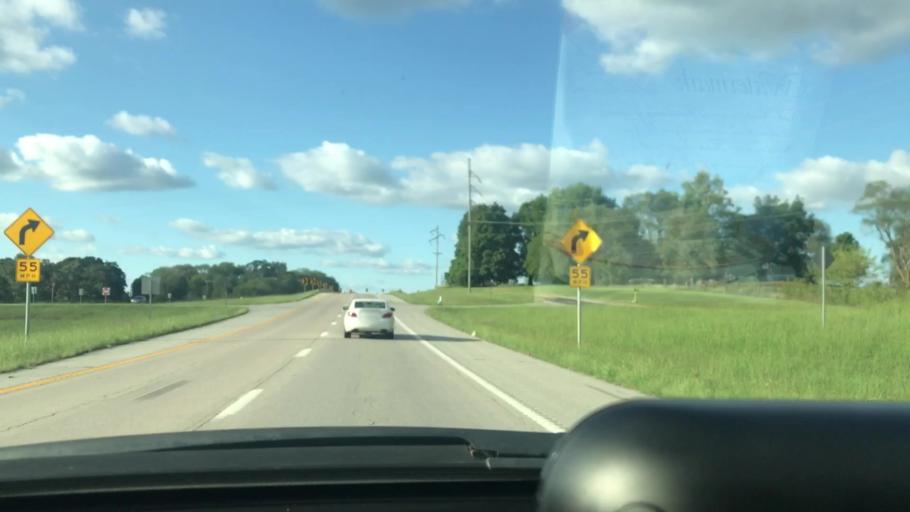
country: US
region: Missouri
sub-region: Pettis County
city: Sedalia
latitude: 38.6332
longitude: -93.2673
